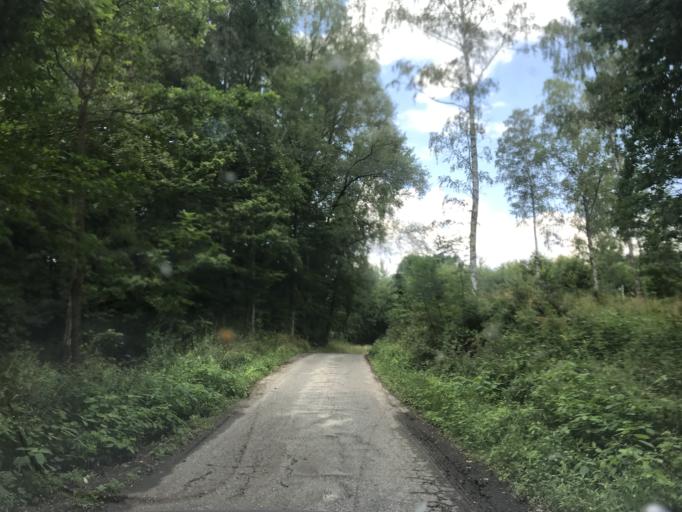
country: PL
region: West Pomeranian Voivodeship
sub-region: Powiat stargardzki
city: Insko
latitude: 53.4856
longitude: 15.5037
